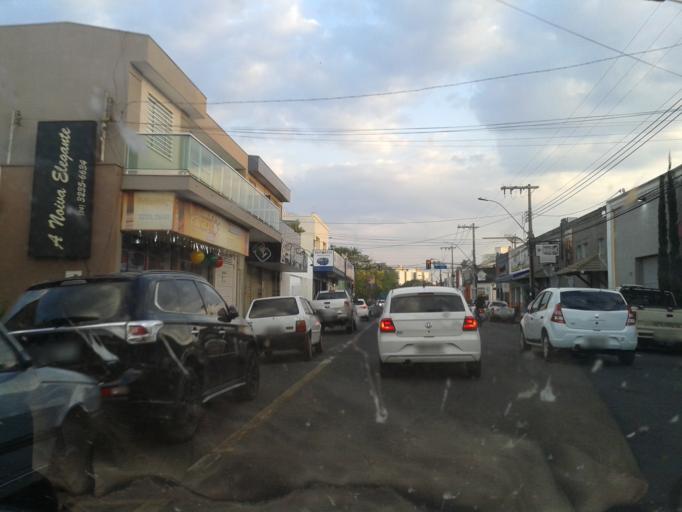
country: BR
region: Minas Gerais
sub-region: Uberlandia
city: Uberlandia
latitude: -18.9093
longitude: -48.2776
